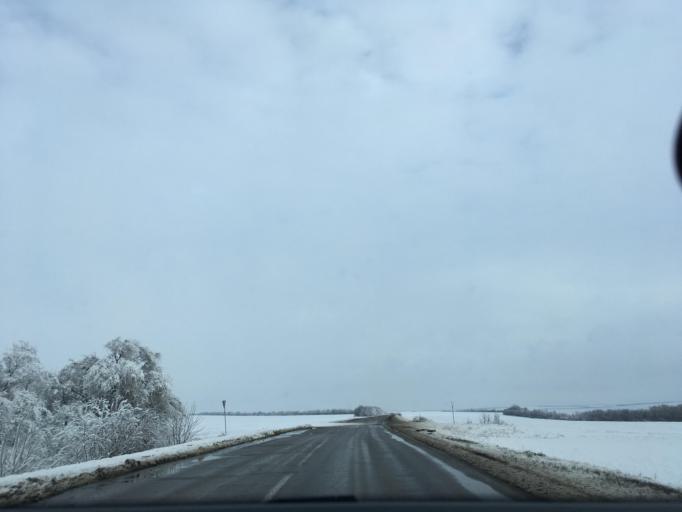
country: UA
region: Luhansk
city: Lozno-Oleksandrivka
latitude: 49.9925
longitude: 39.0255
